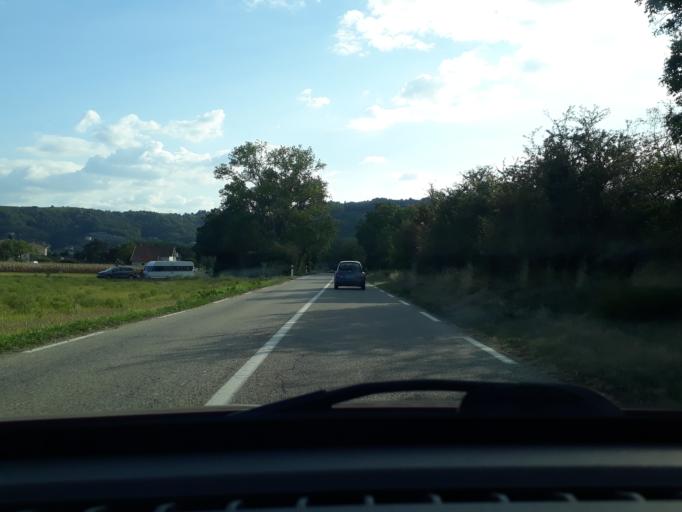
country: FR
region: Rhone-Alpes
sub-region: Departement de l'Isere
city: Sablons
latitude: 45.3318
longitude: 4.7712
